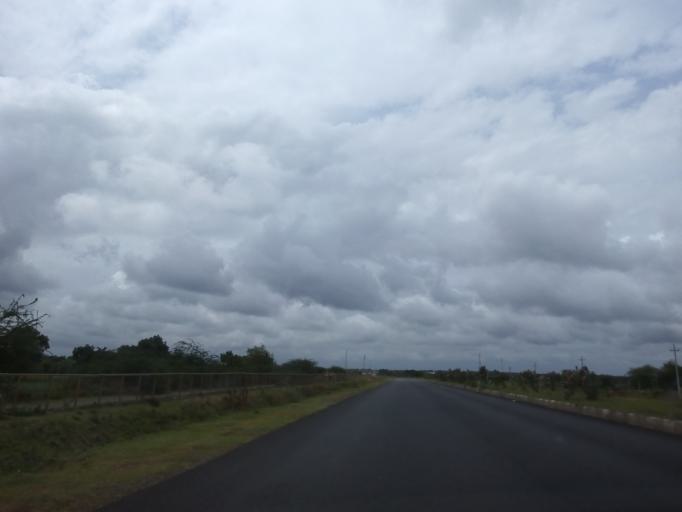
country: IN
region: Karnataka
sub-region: Haveri
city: Byadgi
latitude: 14.6872
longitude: 75.5371
